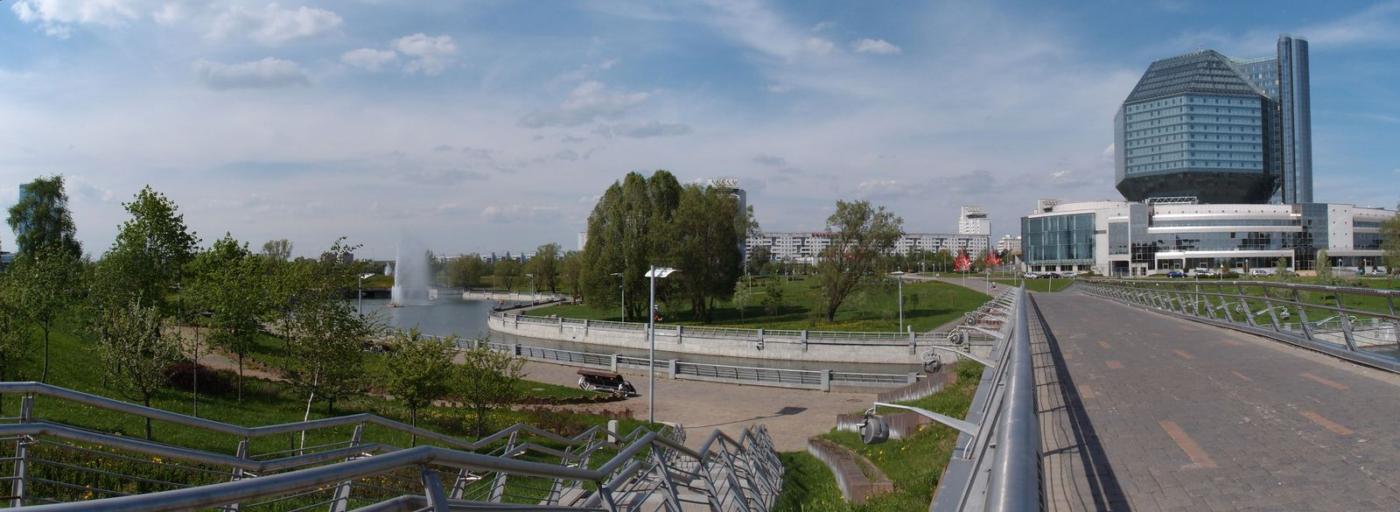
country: BY
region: Minsk
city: Borovlyany
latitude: 53.9293
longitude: 27.6439
